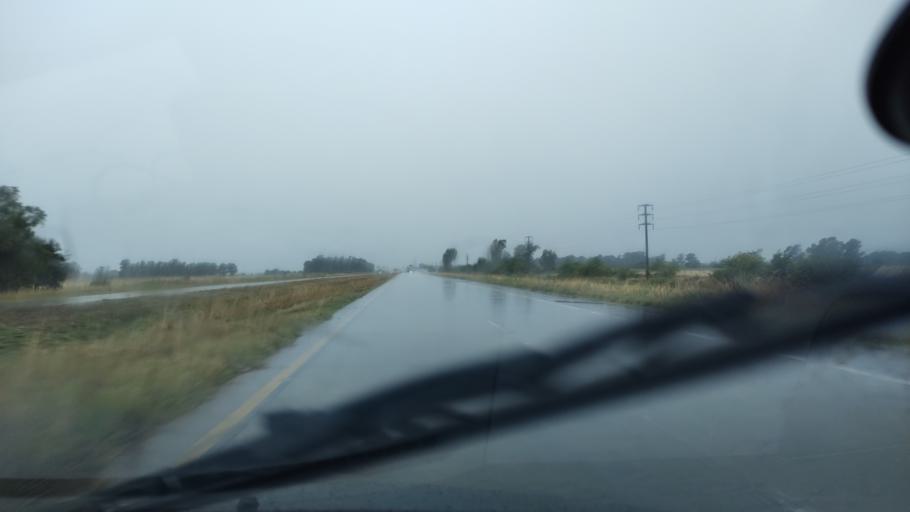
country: AR
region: Buenos Aires
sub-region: Partido de San Vicente
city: San Vicente
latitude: -35.0694
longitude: -58.5161
